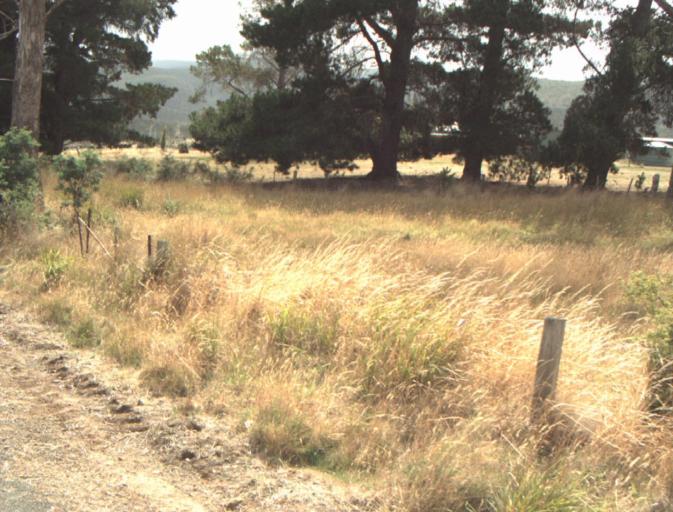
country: AU
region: Tasmania
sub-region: Northern Midlands
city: Evandale
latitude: -41.5046
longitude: 147.3576
